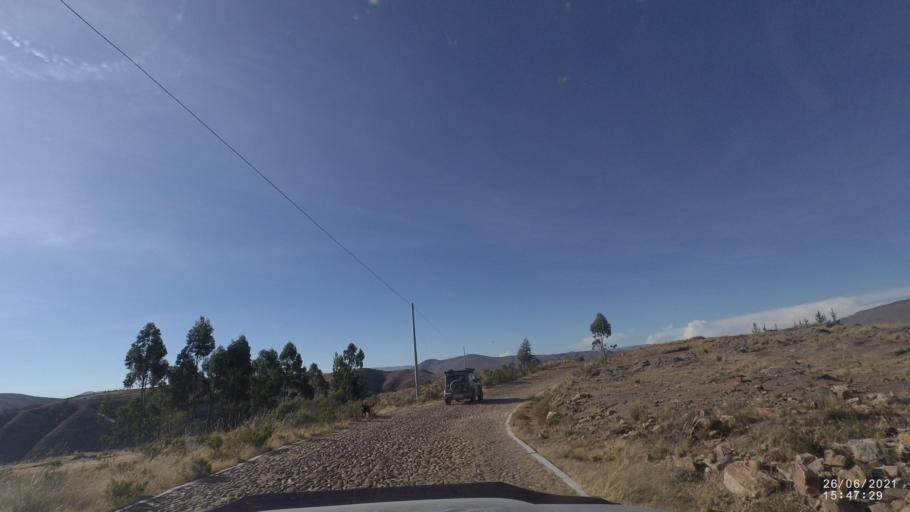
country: BO
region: Cochabamba
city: Arani
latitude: -17.8694
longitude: -65.6989
